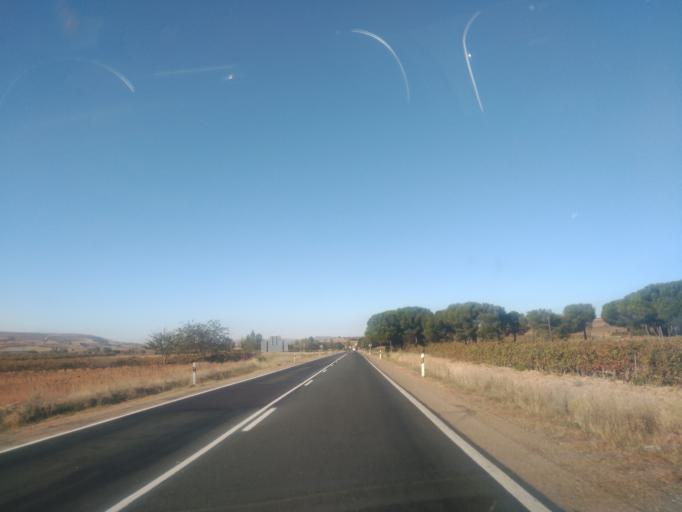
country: ES
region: Castille and Leon
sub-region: Provincia de Burgos
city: Fuentelisendo
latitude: 41.6245
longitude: -3.8862
